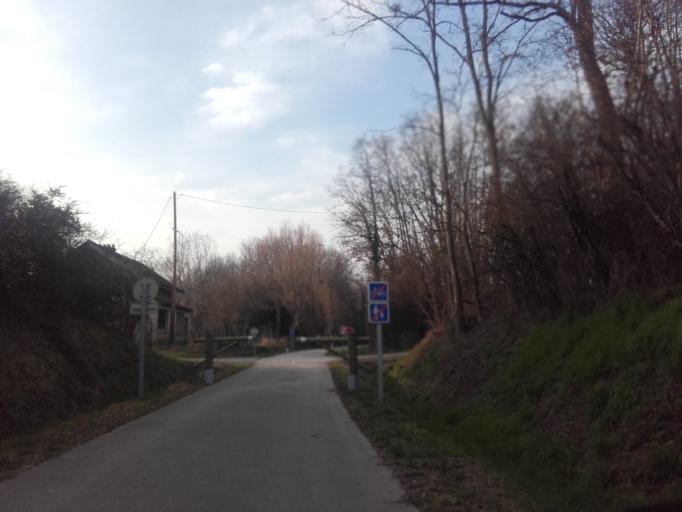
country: FR
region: Bourgogne
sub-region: Departement de la Cote-d'Or
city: Nolay
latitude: 46.9088
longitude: 4.6466
